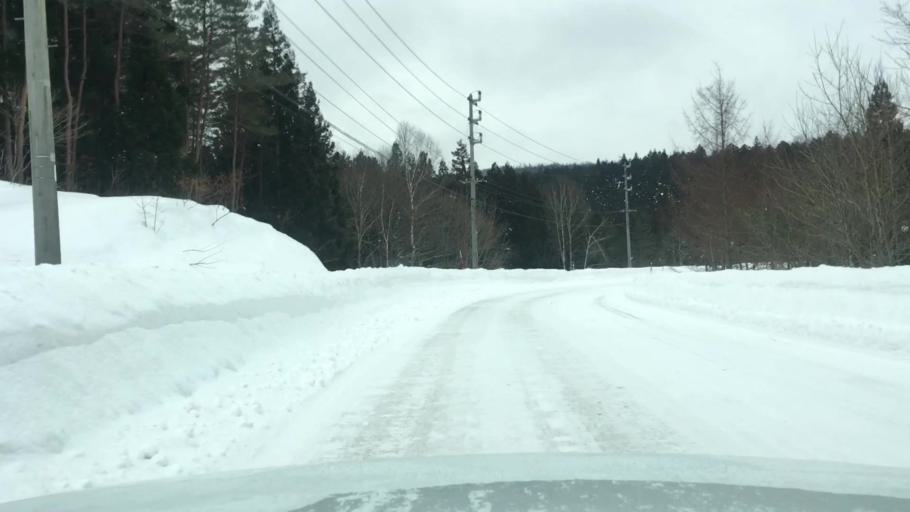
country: JP
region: Akita
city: Hanawa
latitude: 39.9951
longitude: 140.9931
